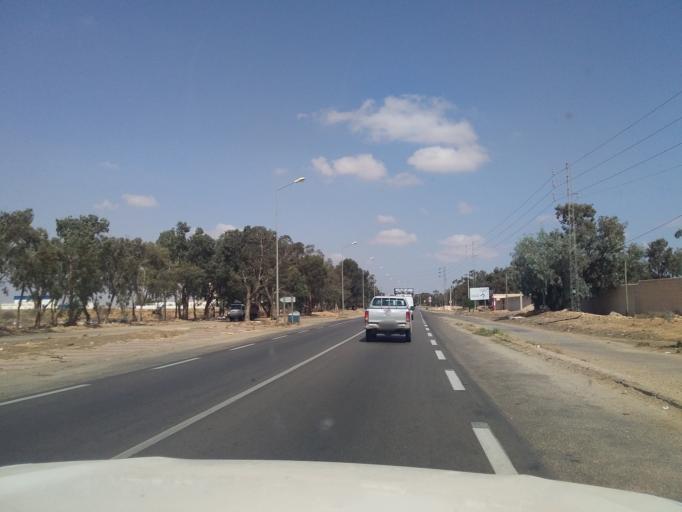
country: TN
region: Madanin
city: Medenine
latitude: 33.5965
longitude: 10.3106
